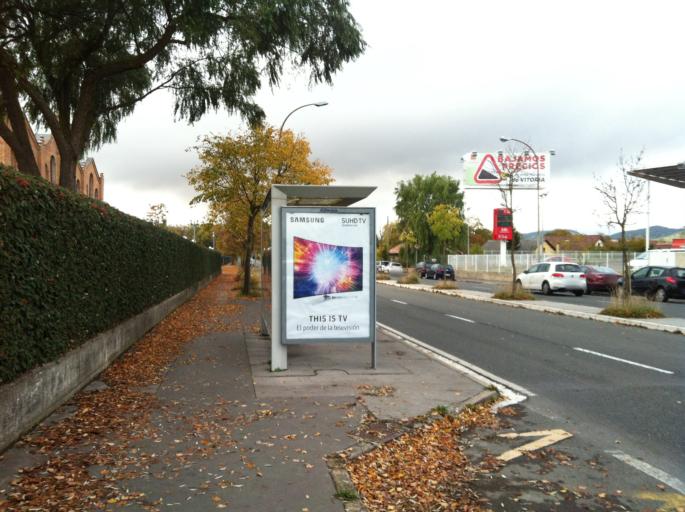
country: ES
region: Basque Country
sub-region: Provincia de Alava
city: Gasteiz / Vitoria
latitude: 42.8571
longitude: -2.7174
